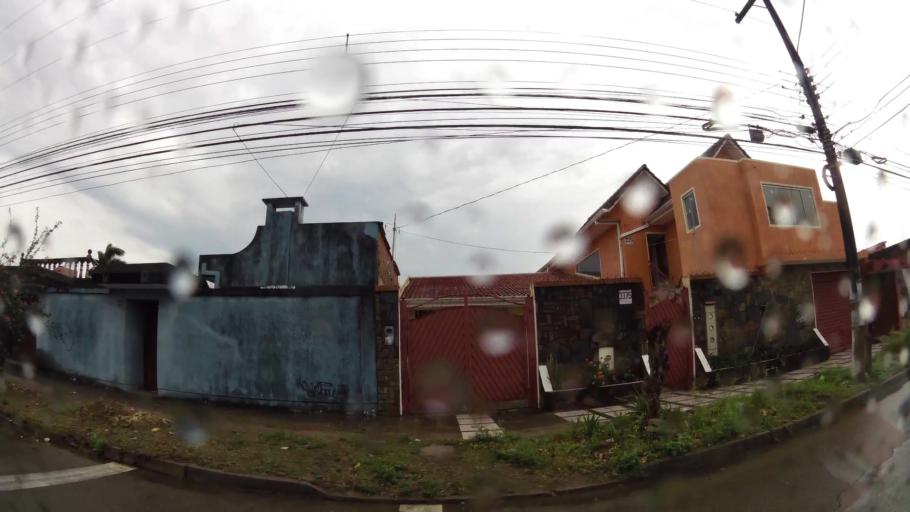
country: BO
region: Santa Cruz
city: Santa Cruz de la Sierra
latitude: -17.7643
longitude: -63.1550
